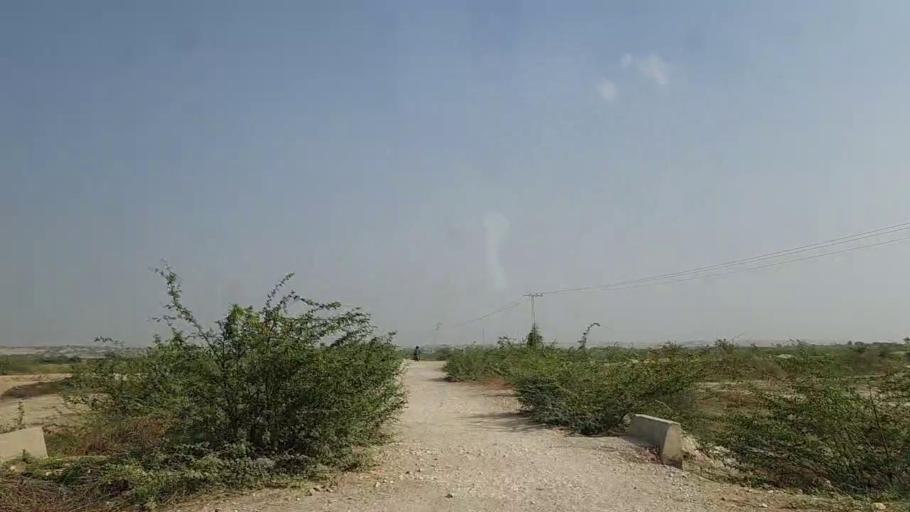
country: PK
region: Sindh
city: Naukot
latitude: 24.6647
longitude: 69.2798
